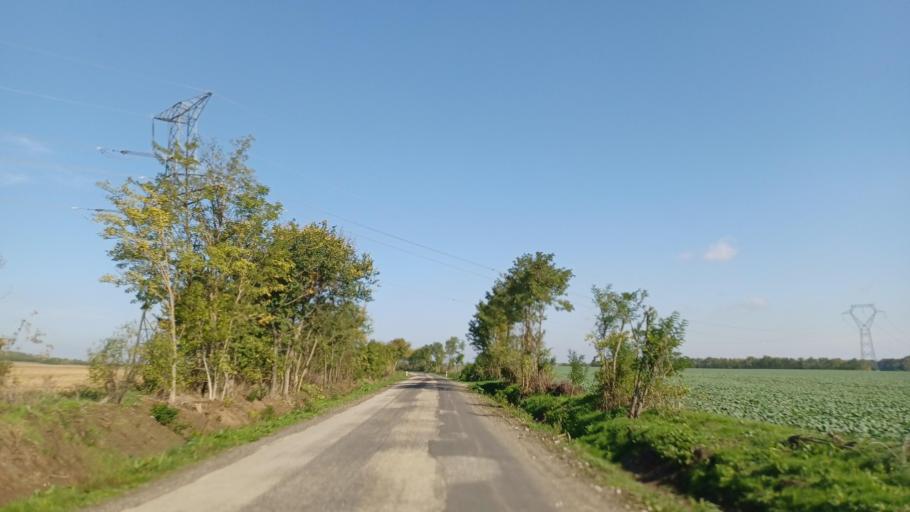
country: HU
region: Tolna
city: Nagydorog
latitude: 46.5808
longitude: 18.5947
